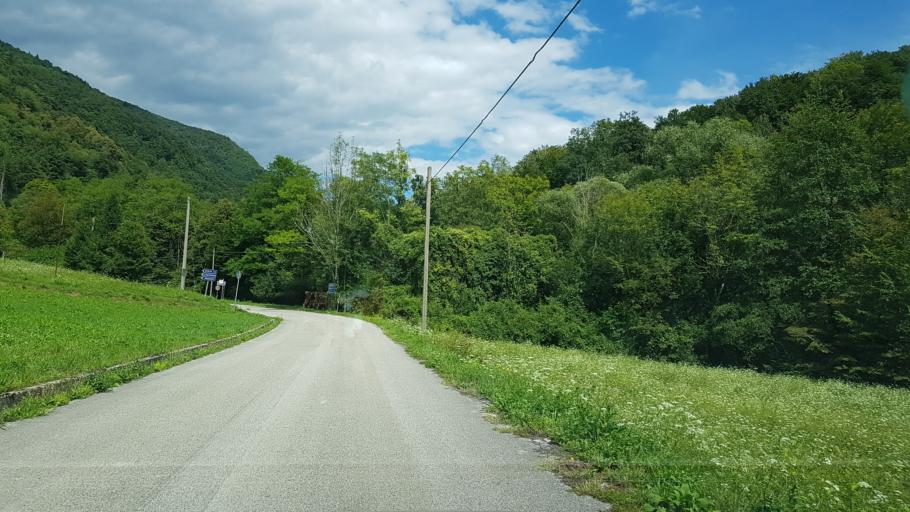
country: IT
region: Friuli Venezia Giulia
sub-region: Provincia di Udine
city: Stregna
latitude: 46.0963
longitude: 13.5780
